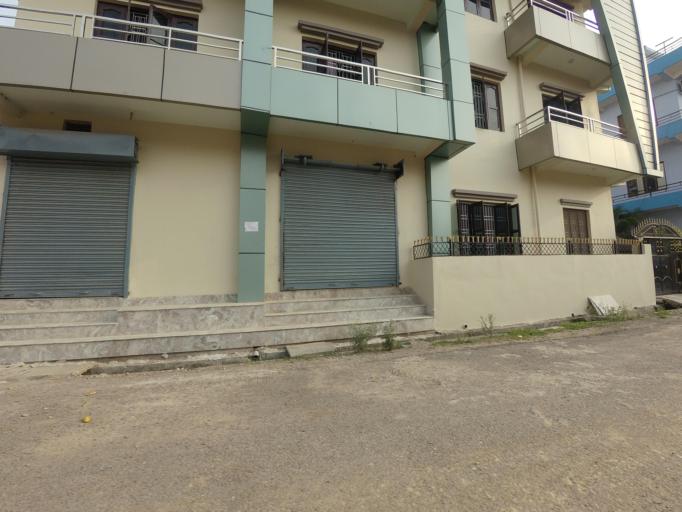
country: NP
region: Western Region
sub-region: Lumbini Zone
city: Bhairahawa
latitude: 27.5077
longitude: 83.4606
